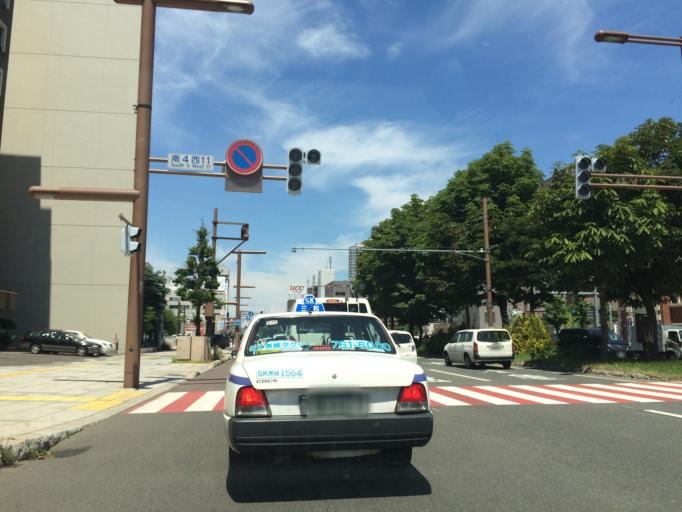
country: JP
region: Hokkaido
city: Sapporo
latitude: 43.0543
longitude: 141.3419
